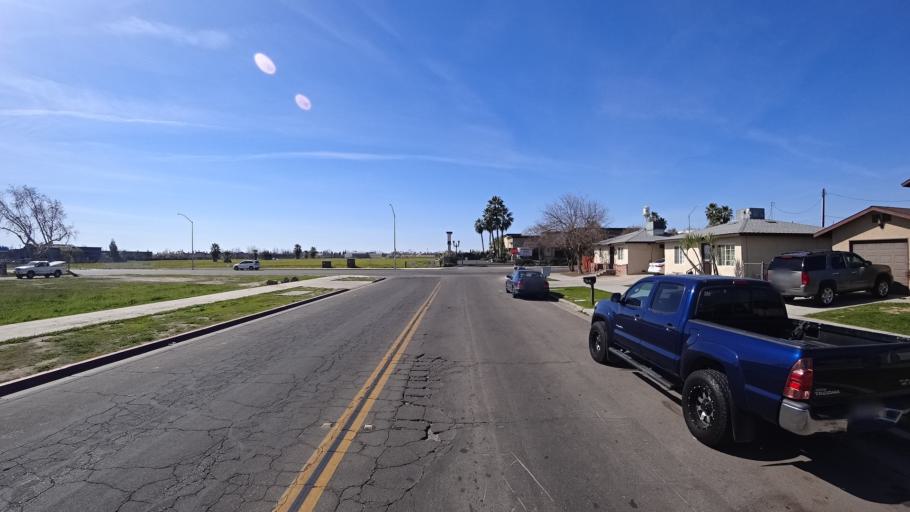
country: US
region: California
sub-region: Fresno County
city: Fresno
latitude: 36.8426
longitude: -119.8013
